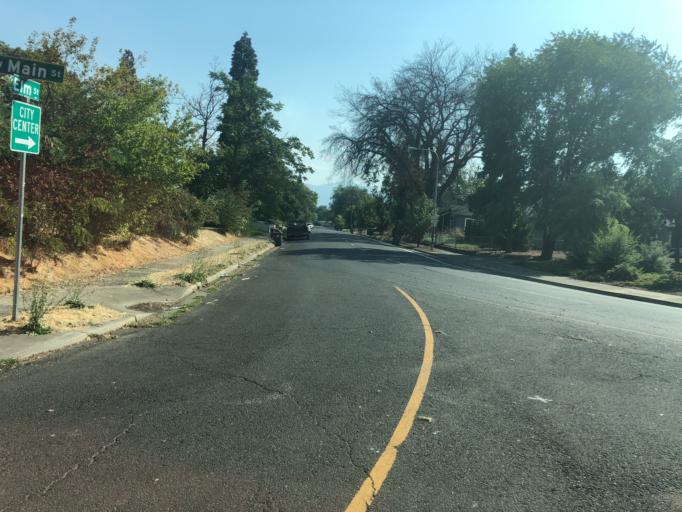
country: US
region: Oregon
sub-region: Jackson County
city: Medford
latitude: 42.3236
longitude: -122.8897
